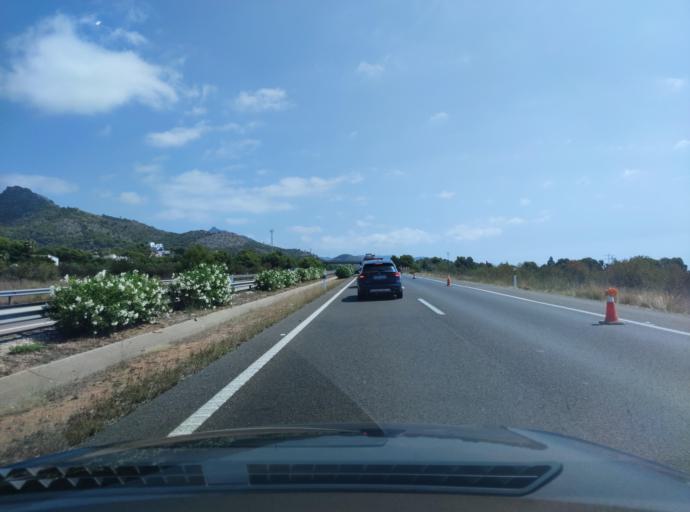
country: ES
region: Valencia
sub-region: Provincia de Castello
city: Benicassim
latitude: 40.0404
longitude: 0.0210
